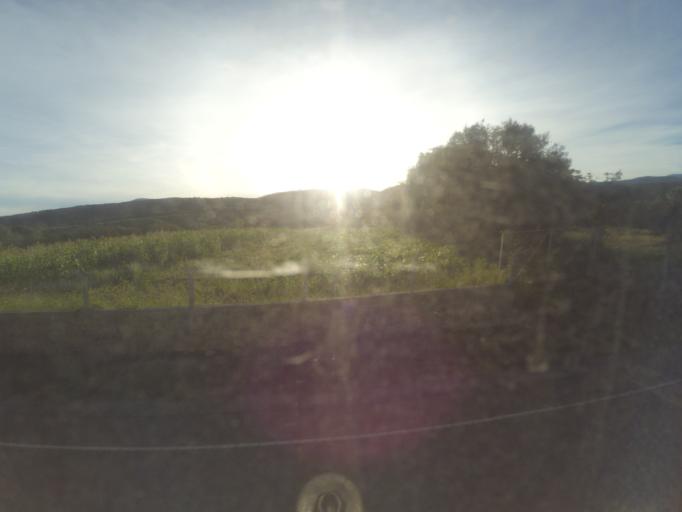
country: BO
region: Tarija
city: Tarija
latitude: -21.5233
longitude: -64.5745
